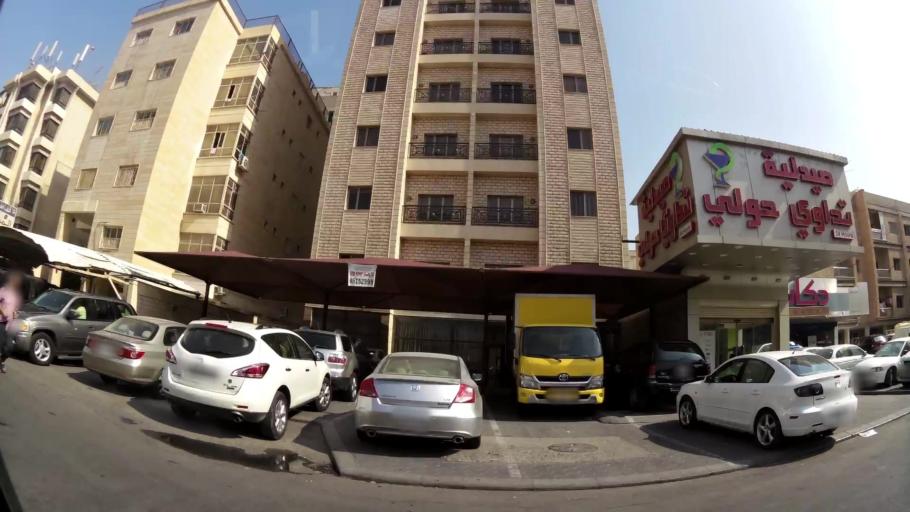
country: KW
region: Muhafazat Hawalli
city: Hawalli
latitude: 29.3349
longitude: 48.0322
